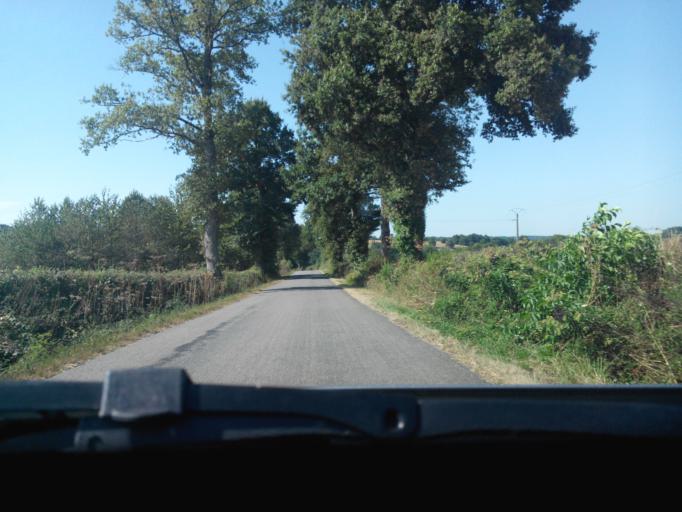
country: FR
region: Poitou-Charentes
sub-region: Departement de la Charente
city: Brigueuil
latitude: 45.9676
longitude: 0.7922
